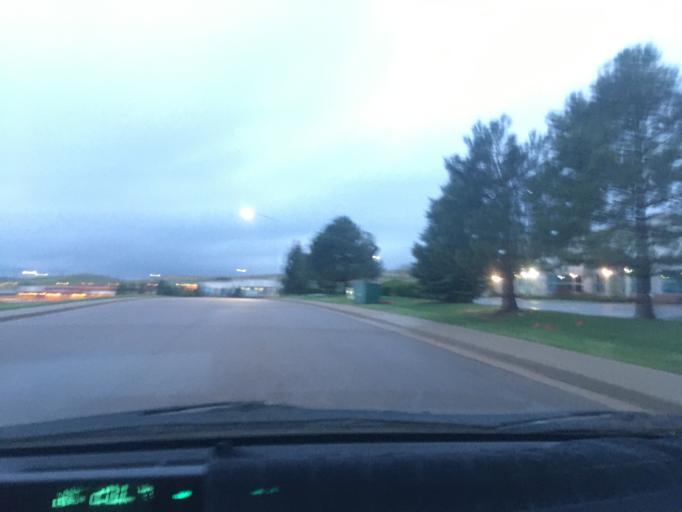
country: US
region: Colorado
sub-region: Broomfield County
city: Broomfield
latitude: 39.9051
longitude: -105.0992
